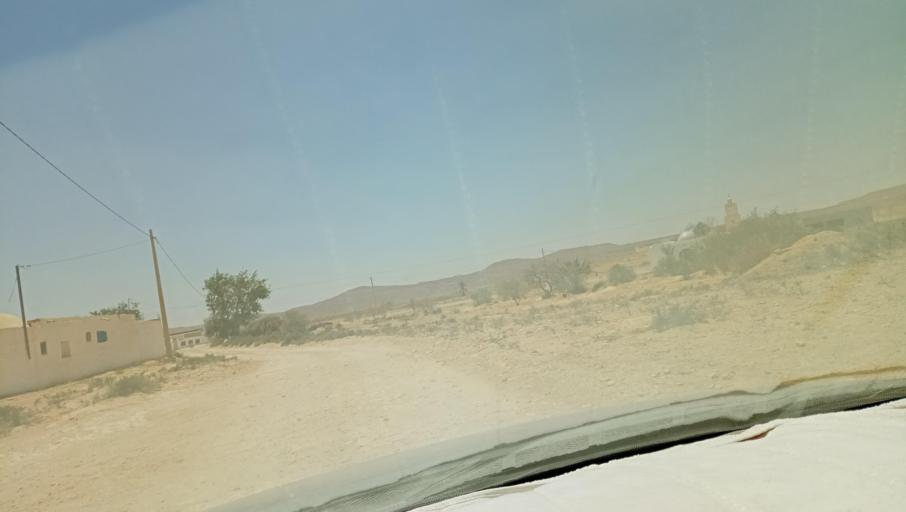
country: TN
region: Tataouine
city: Tataouine
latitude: 32.8531
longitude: 10.5343
